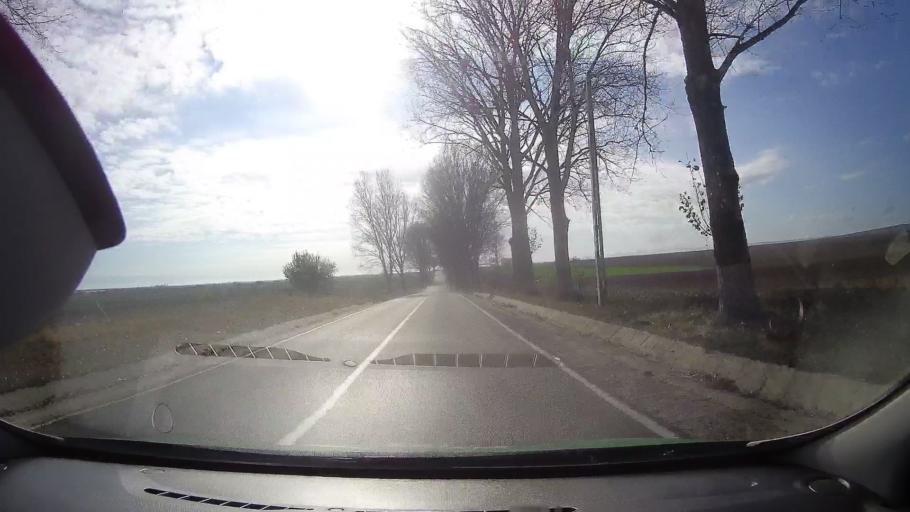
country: RO
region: Tulcea
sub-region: Comuna Valea Nucarilor
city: Agighiol
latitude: 45.0032
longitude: 28.8856
